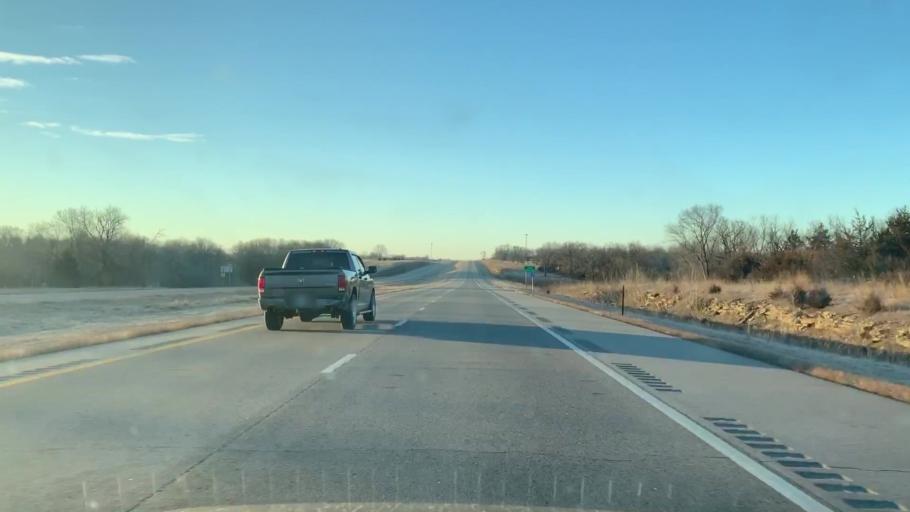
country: US
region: Kansas
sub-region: Linn County
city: La Cygne
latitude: 38.3900
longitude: -94.6878
